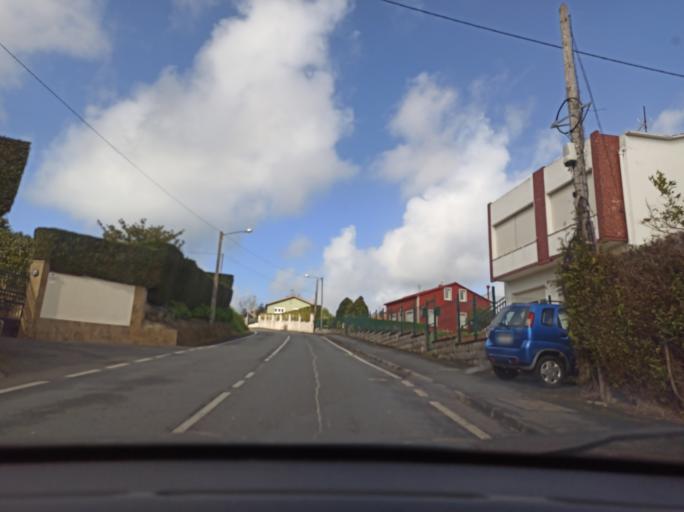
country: ES
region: Galicia
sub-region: Provincia da Coruna
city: Cambre
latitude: 43.3255
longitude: -8.3536
